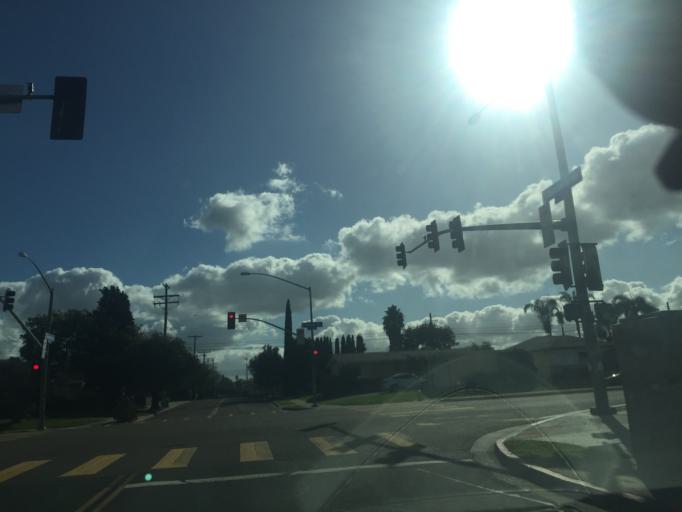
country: US
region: California
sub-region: San Diego County
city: La Mesa
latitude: 32.7951
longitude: -117.0787
